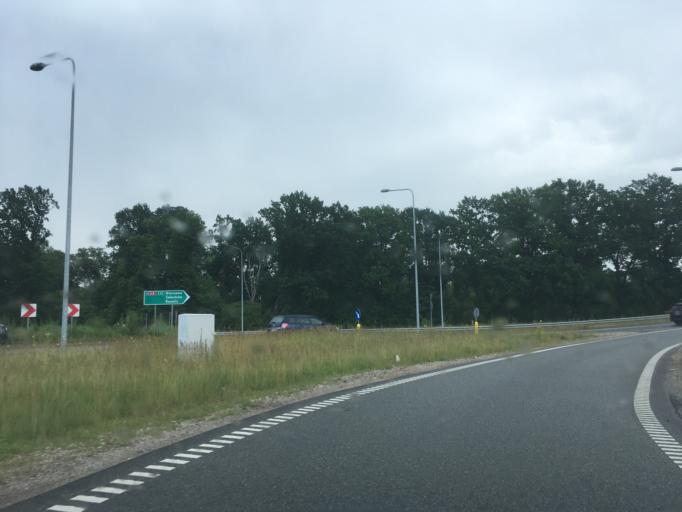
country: PL
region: Lodz Voivodeship
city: Zabia Wola
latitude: 52.0526
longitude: 20.7159
